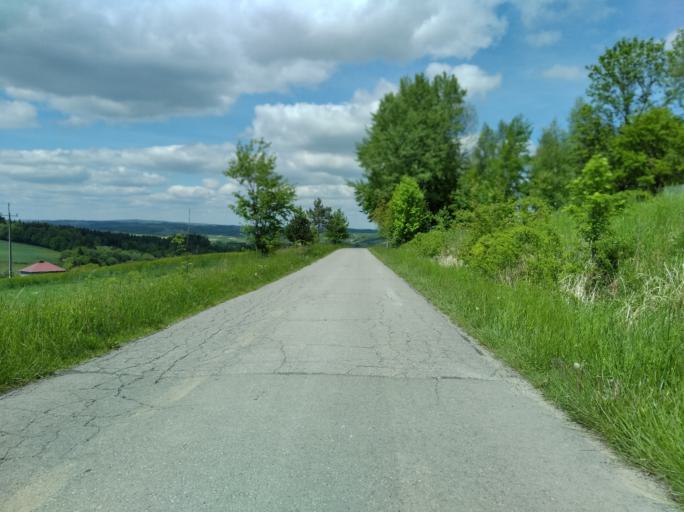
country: PL
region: Subcarpathian Voivodeship
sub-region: Powiat ropczycko-sedziszowski
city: Wielopole Skrzynskie
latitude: 49.9252
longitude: 21.6046
